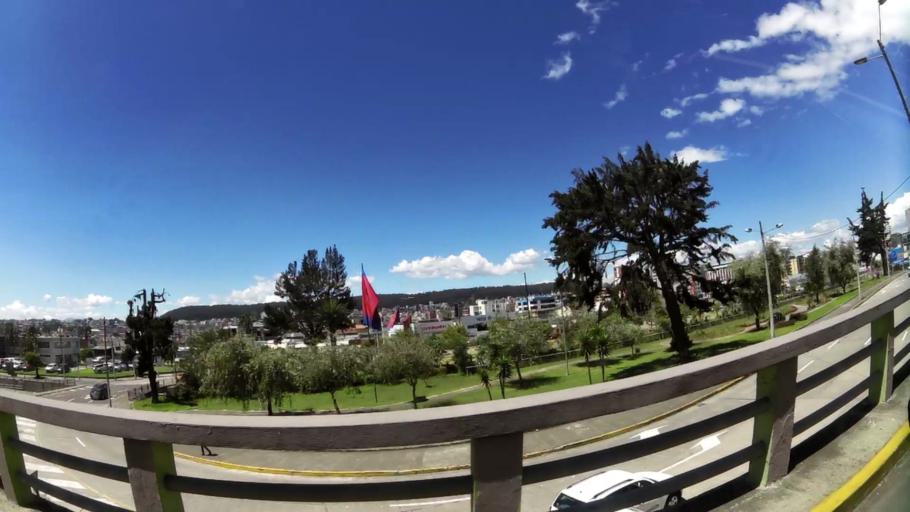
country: EC
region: Pichincha
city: Quito
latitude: -0.1667
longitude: -78.4872
